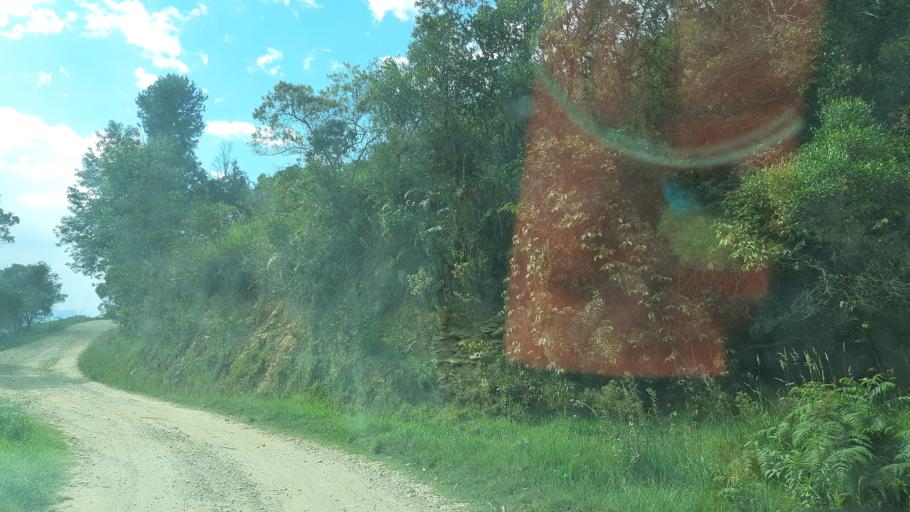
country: CO
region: Boyaca
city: Santa Sofia
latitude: 5.7203
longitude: -73.5394
